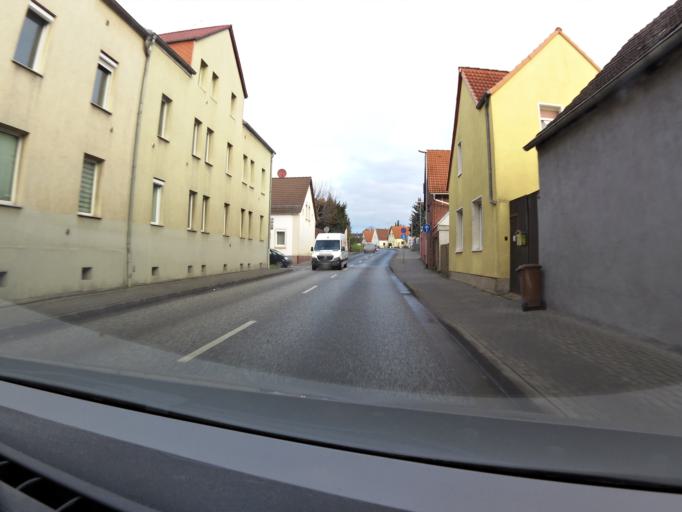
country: DE
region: Saxony-Anhalt
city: Diesdorf
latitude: 52.1316
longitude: 11.5736
